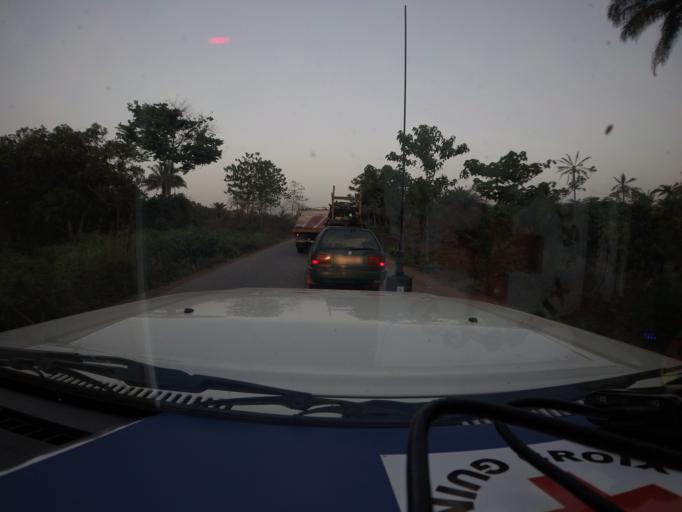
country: GN
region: Kindia
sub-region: Kindia
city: Kindia
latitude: 9.9037
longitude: -13.0075
